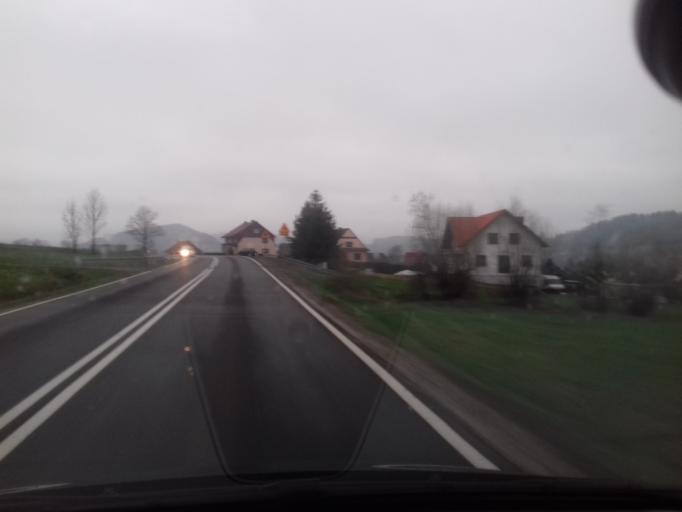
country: PL
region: Lesser Poland Voivodeship
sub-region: Powiat limanowski
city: Tymbark
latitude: 49.7284
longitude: 20.2948
